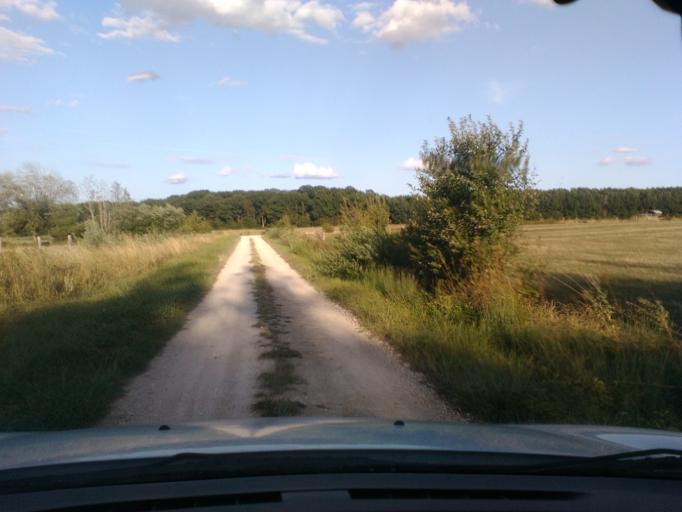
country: FR
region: Lorraine
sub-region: Departement des Vosges
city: Mirecourt
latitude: 48.3457
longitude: 6.0299
